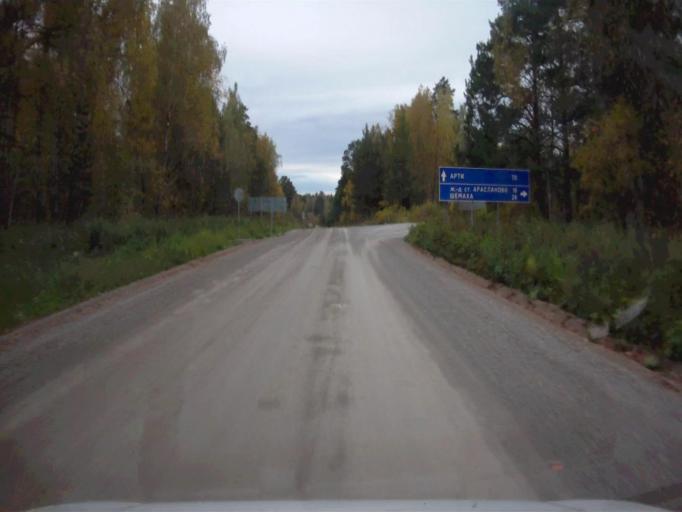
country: RU
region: Chelyabinsk
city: Nyazepetrovsk
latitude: 56.0860
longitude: 59.4189
